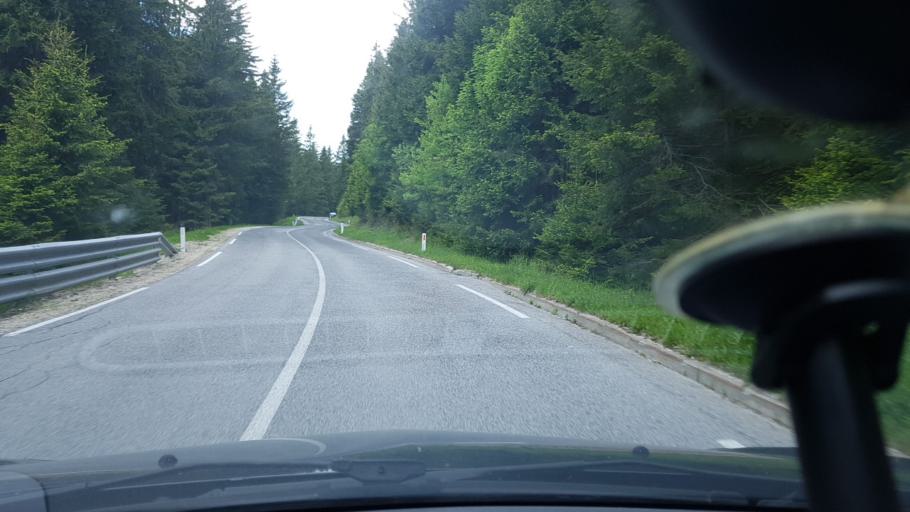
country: SI
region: Vitanje
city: Vitanje
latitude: 46.4470
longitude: 15.3318
